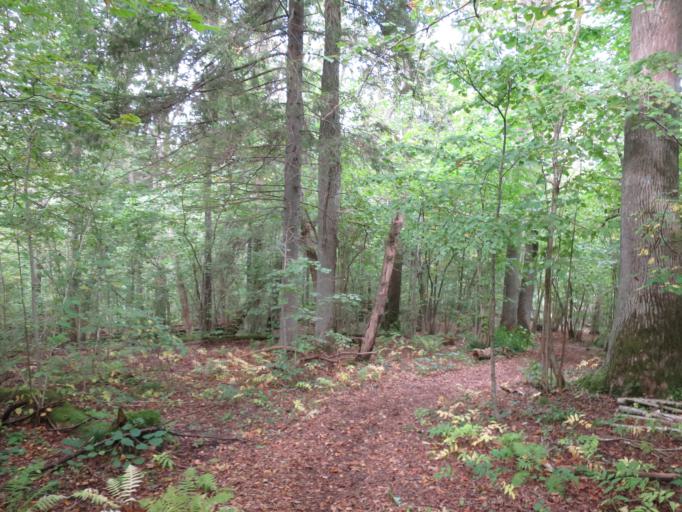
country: LV
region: Sigulda
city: Sigulda
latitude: 57.1720
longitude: 24.8312
